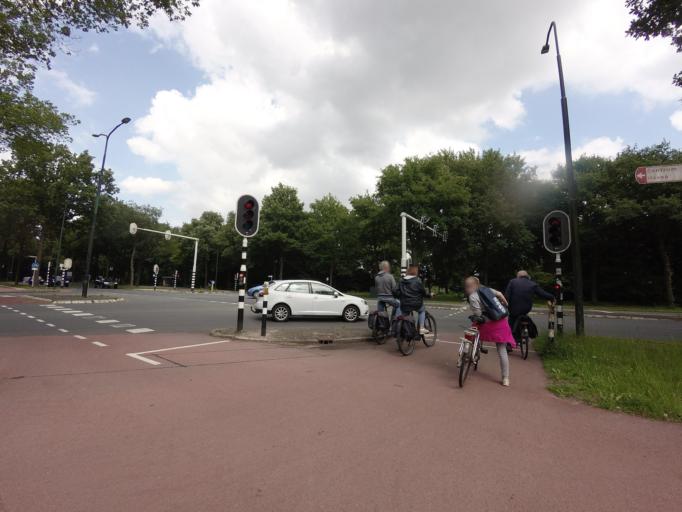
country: NL
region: North Holland
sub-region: Gemeente Huizen
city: Huizen
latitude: 52.2903
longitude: 5.2579
